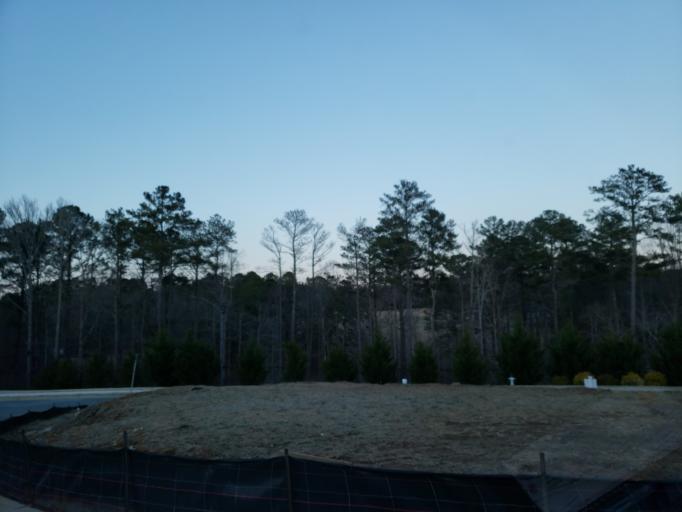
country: US
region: Georgia
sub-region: Cherokee County
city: Woodstock
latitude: 34.0984
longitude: -84.4956
